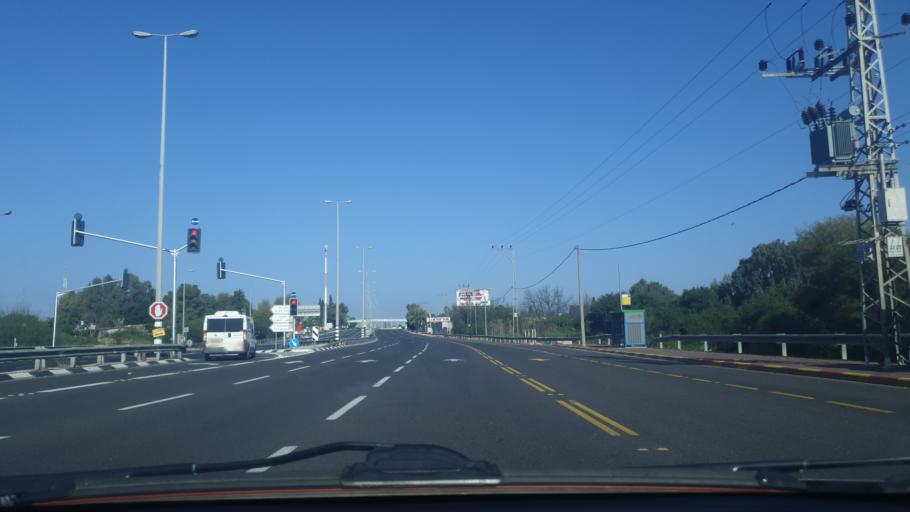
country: IL
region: Central District
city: Bet Dagan
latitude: 32.0009
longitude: 34.8214
